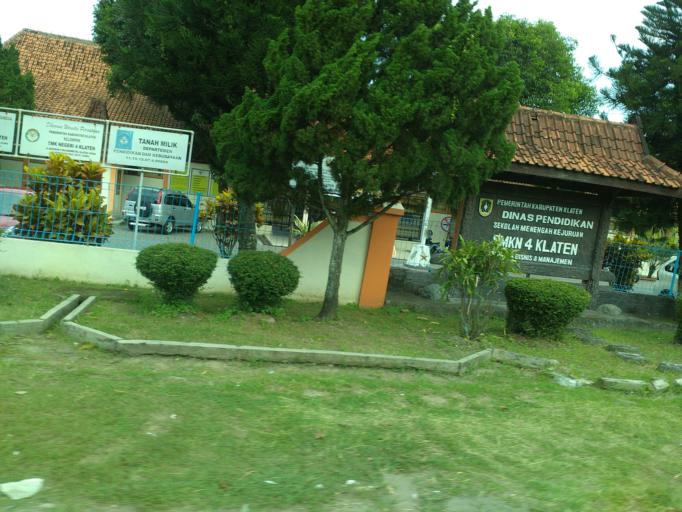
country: ID
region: Central Java
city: Klaten
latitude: -7.6889
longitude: 110.6342
